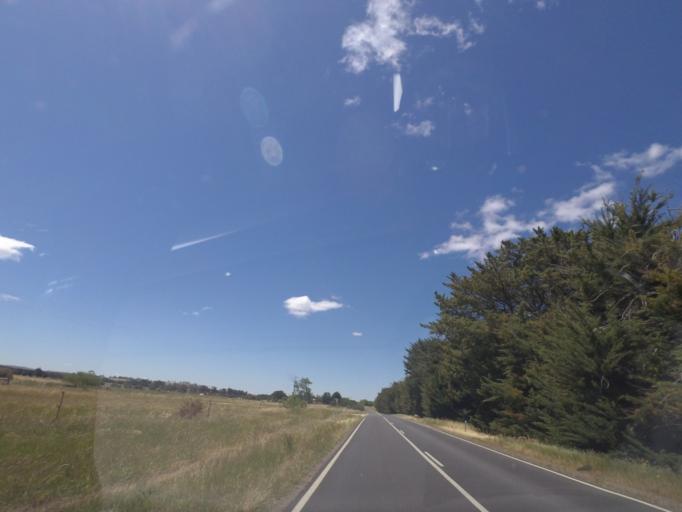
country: AU
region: Victoria
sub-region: Mount Alexander
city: Castlemaine
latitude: -37.2450
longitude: 144.3237
